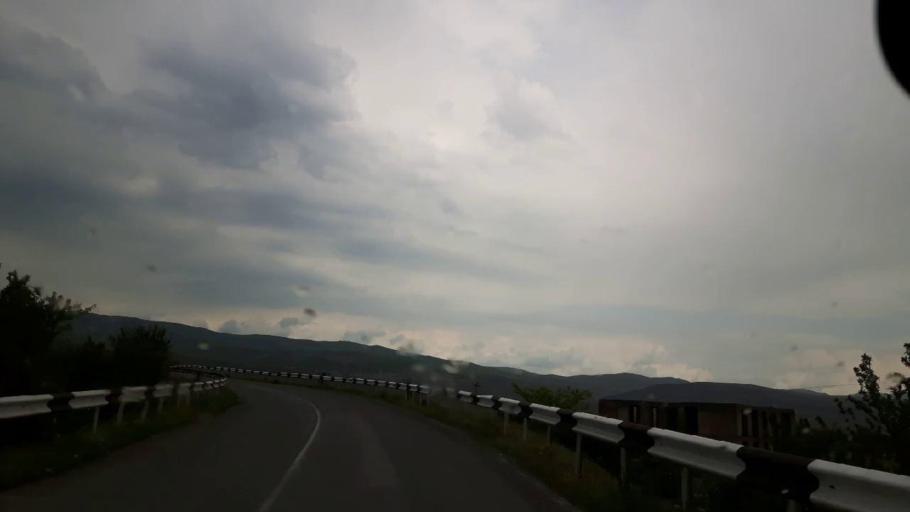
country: GE
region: Shida Kartli
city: Gori
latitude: 41.9637
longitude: 44.1857
